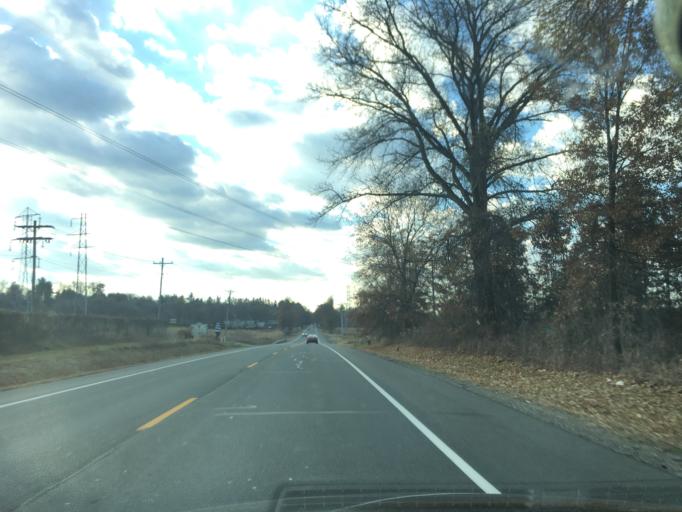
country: US
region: New York
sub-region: Albany County
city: Menands
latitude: 42.6705
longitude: -73.6913
